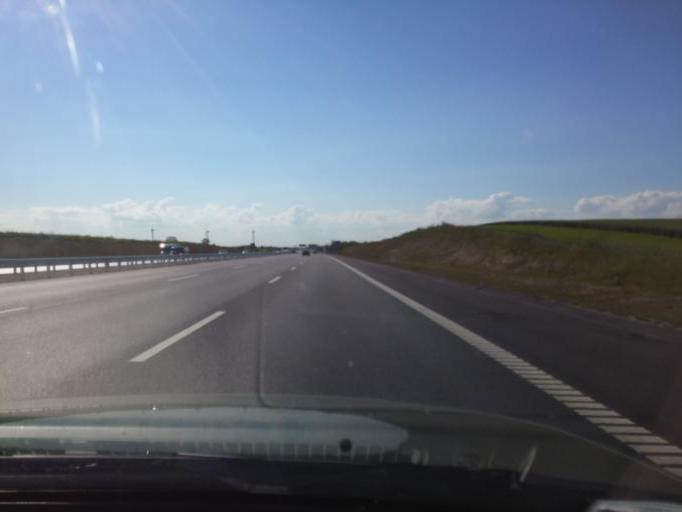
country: DK
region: South Denmark
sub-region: Middelfart Kommune
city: Norre Aby
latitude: 55.4856
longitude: 9.8546
